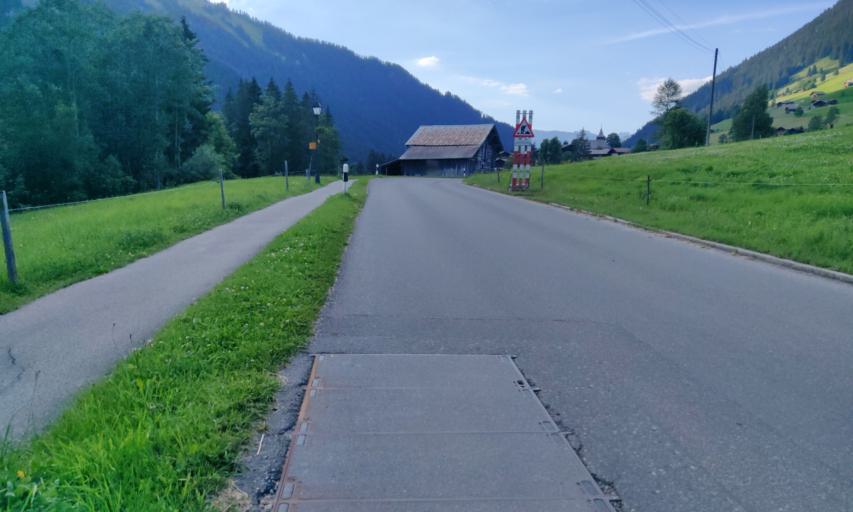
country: CH
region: Bern
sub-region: Obersimmental-Saanen District
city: Gstaad
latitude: 46.4200
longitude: 7.3229
